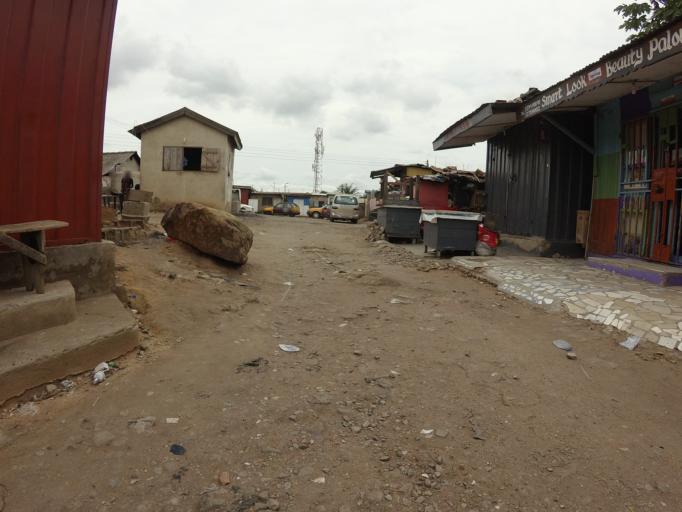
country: GH
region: Greater Accra
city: Accra
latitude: 5.5905
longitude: -0.2148
